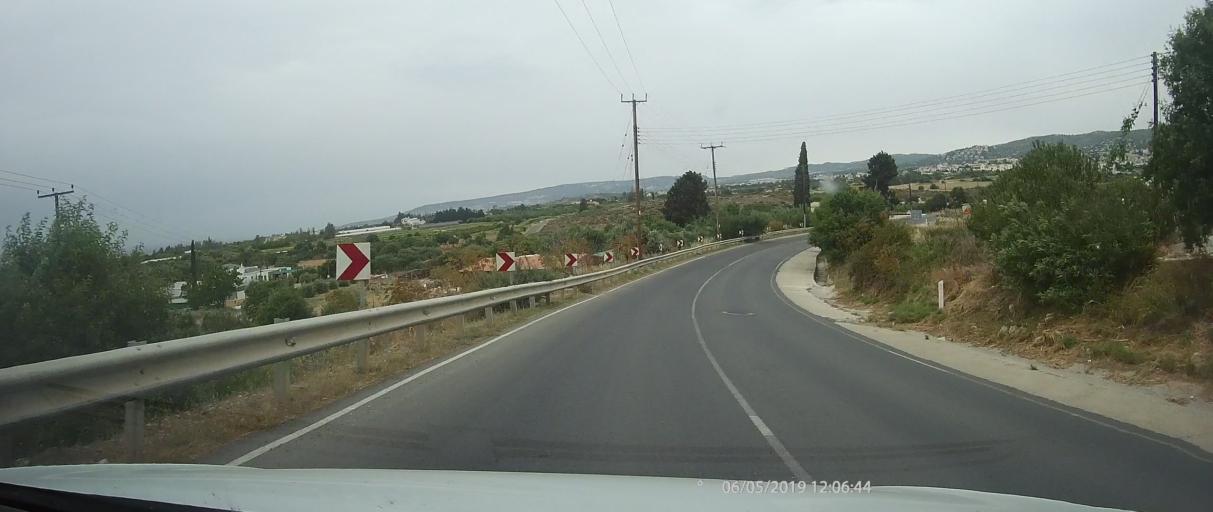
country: CY
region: Pafos
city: Empa
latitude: 34.8200
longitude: 32.4227
